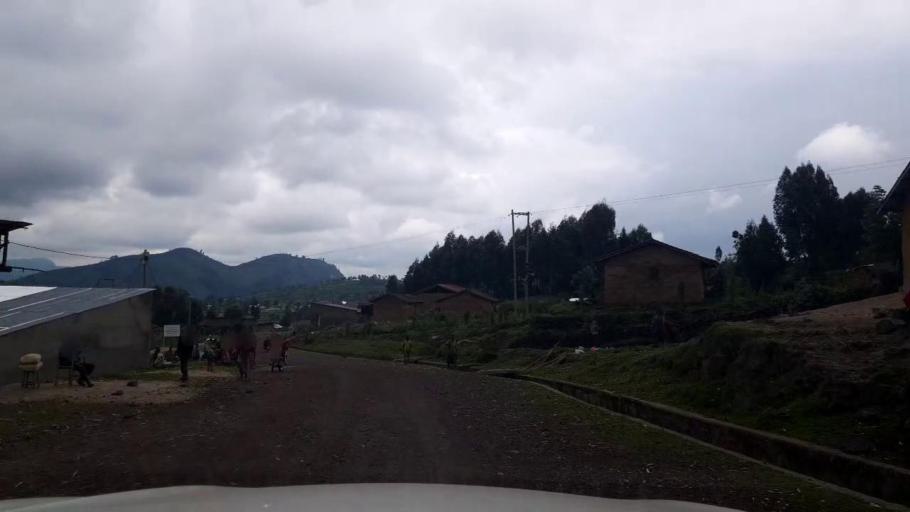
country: RW
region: Northern Province
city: Musanze
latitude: -1.5750
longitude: 29.4903
